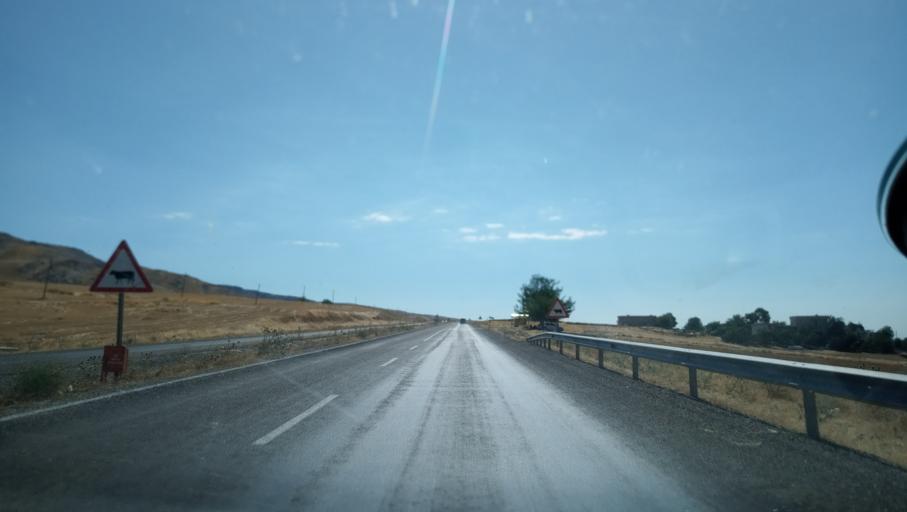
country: TR
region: Diyarbakir
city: Silvan
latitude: 38.1280
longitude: 41.0621
